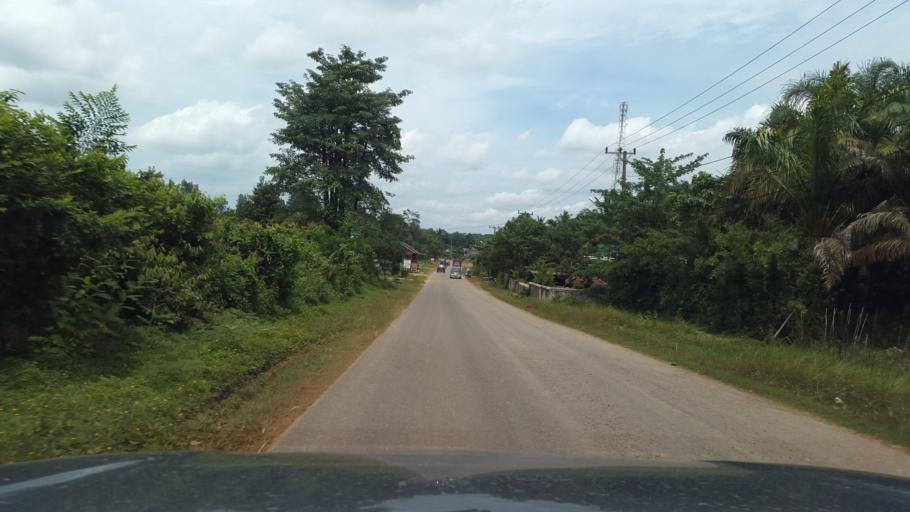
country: ID
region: South Sumatra
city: Gunungmegang Dalam
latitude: -3.3221
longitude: 103.9020
